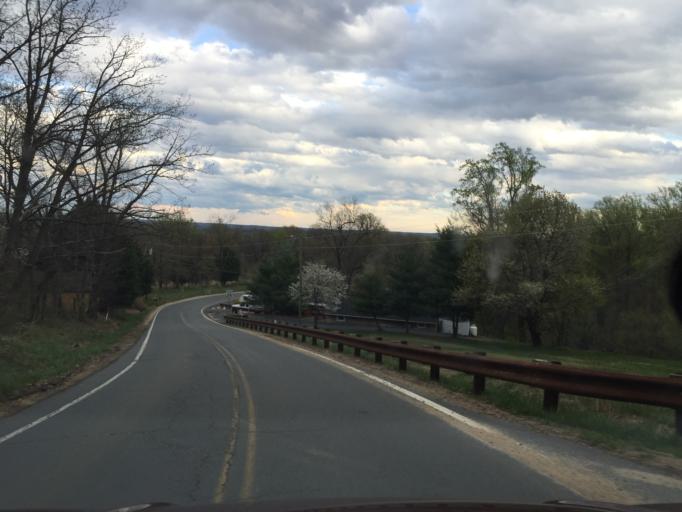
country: US
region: Maryland
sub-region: Frederick County
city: Point of Rocks
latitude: 39.2381
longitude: -77.5587
